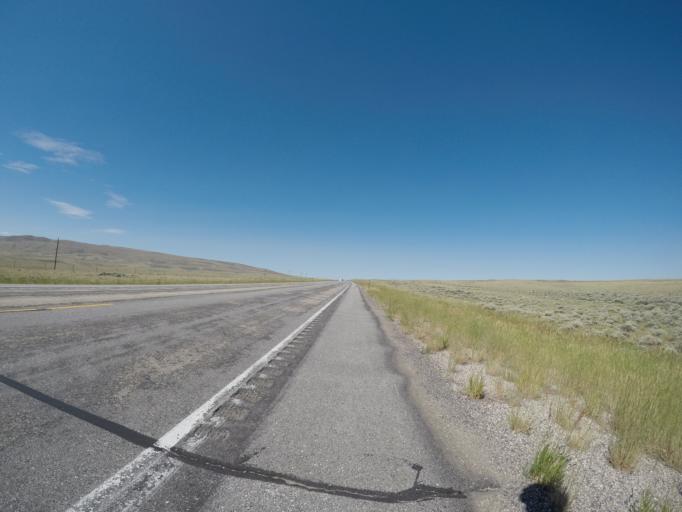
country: US
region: Wyoming
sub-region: Carbon County
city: Saratoga
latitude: 41.8025
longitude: -106.7050
